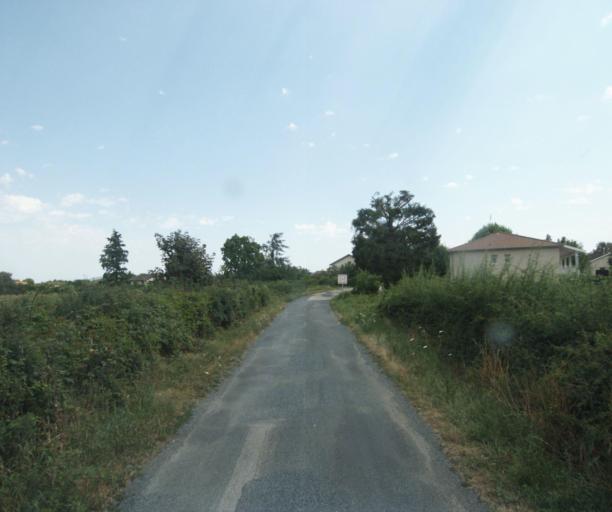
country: FR
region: Rhone-Alpes
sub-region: Departement du Rhone
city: Saint-Germain-Nuelles
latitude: 45.8454
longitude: 4.6010
